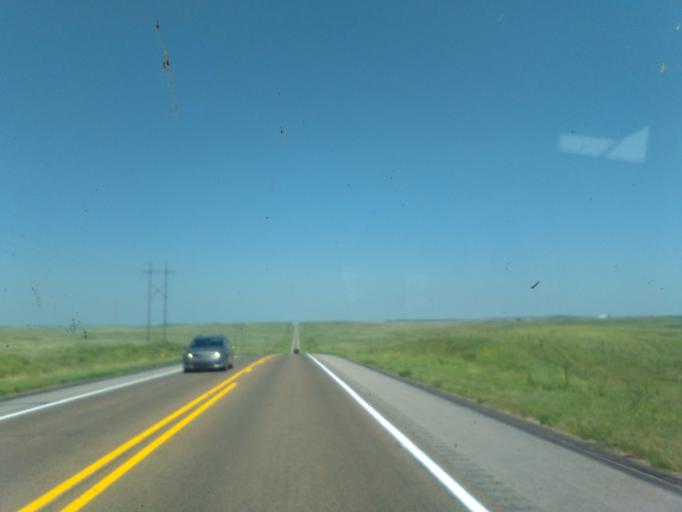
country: US
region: Nebraska
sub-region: Lincoln County
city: North Platte
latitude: 40.8478
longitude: -100.7540
